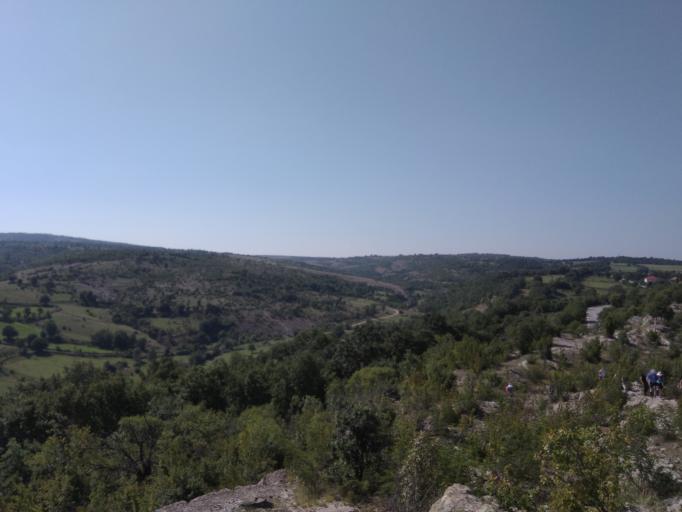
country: BG
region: Kurdzhali
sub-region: Obshtina Krumovgrad
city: Krumovgrad
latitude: 41.5142
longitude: 25.6647
